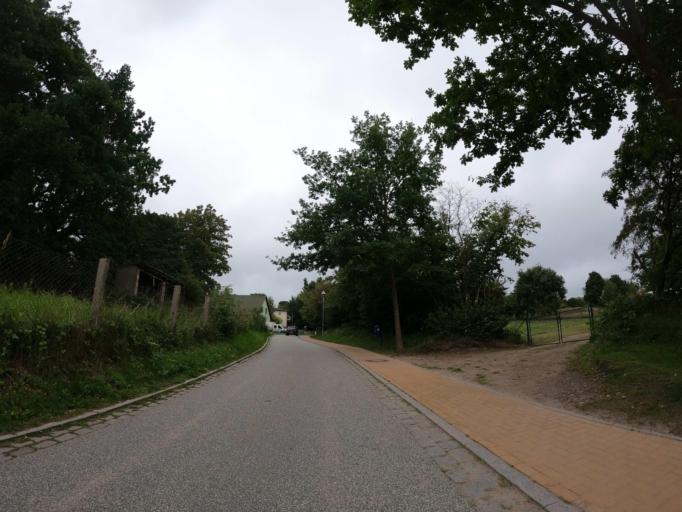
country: DE
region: Mecklenburg-Vorpommern
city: Ostseebad Gohren
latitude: 54.3363
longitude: 13.7399
